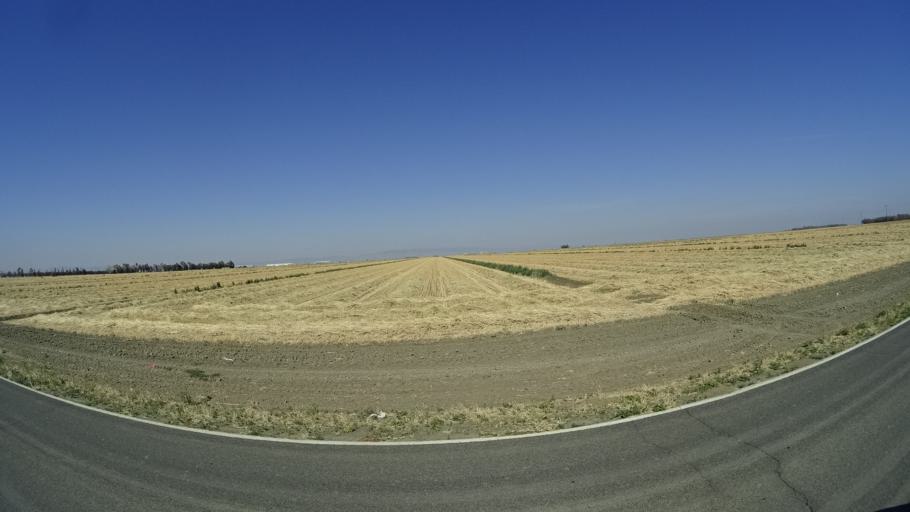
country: US
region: California
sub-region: Kings County
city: Lemoore Station
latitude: 36.3477
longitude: -119.9053
